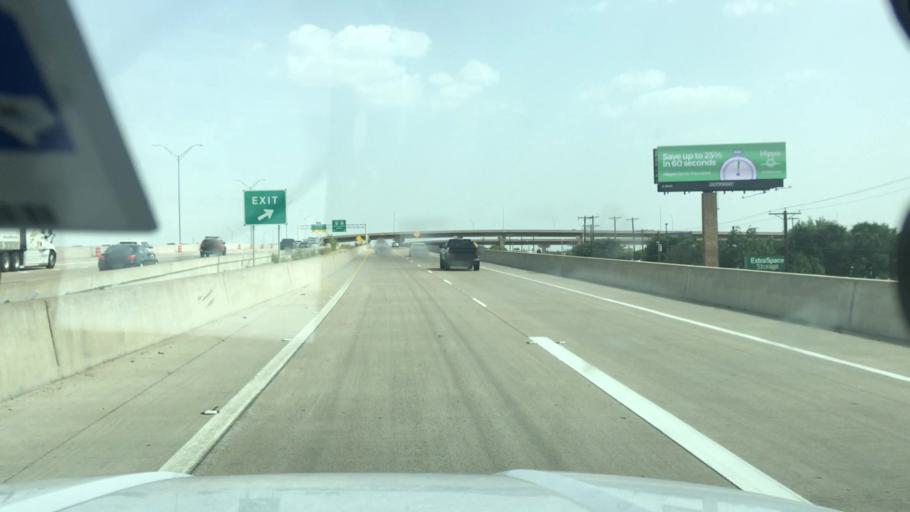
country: US
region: Texas
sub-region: Tarrant County
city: Grapevine
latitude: 32.9342
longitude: -97.0970
